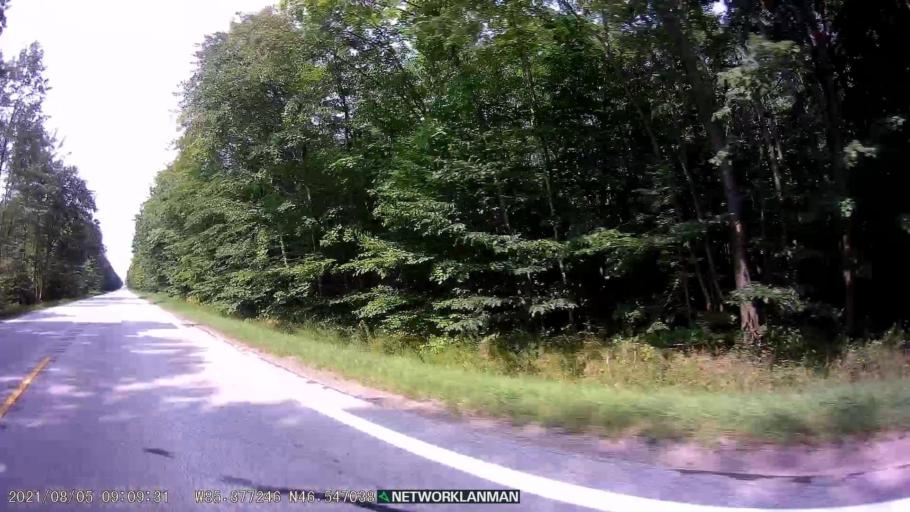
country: US
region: Michigan
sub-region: Luce County
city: Newberry
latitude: 46.5468
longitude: -85.3776
